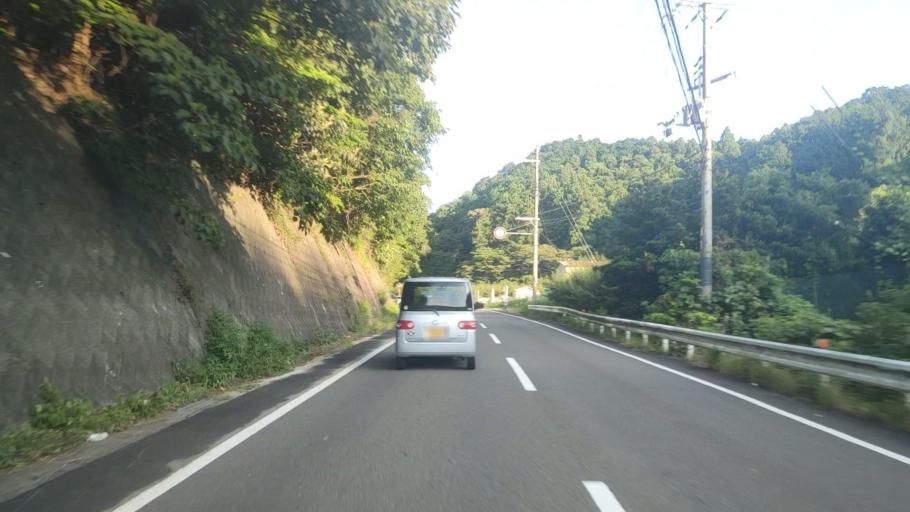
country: JP
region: Wakayama
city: Tanabe
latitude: 33.7326
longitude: 135.4330
